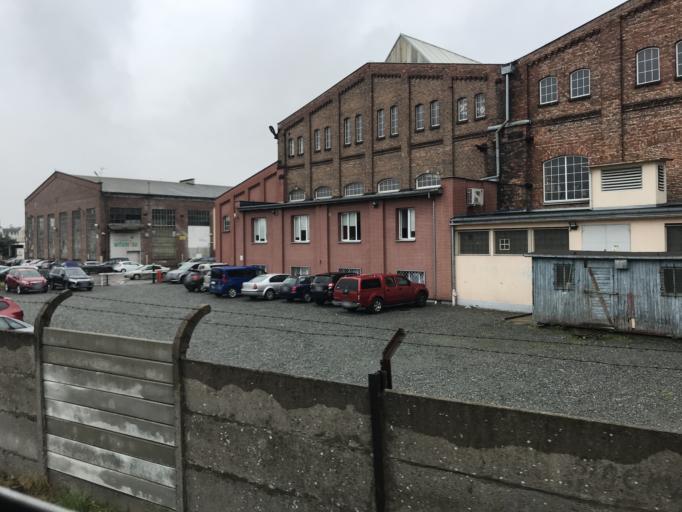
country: PL
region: Warmian-Masurian Voivodeship
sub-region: Powiat elblaski
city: Elblag
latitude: 54.1515
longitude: 19.4082
